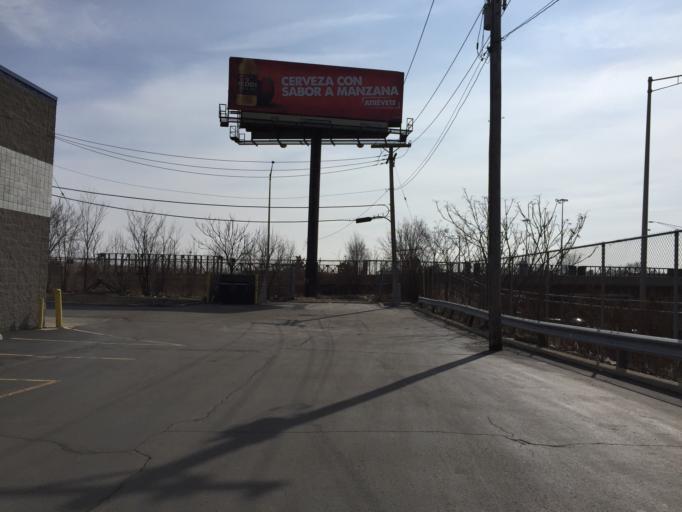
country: US
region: Illinois
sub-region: Cook County
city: Cicero
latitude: 41.8455
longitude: -87.7438
